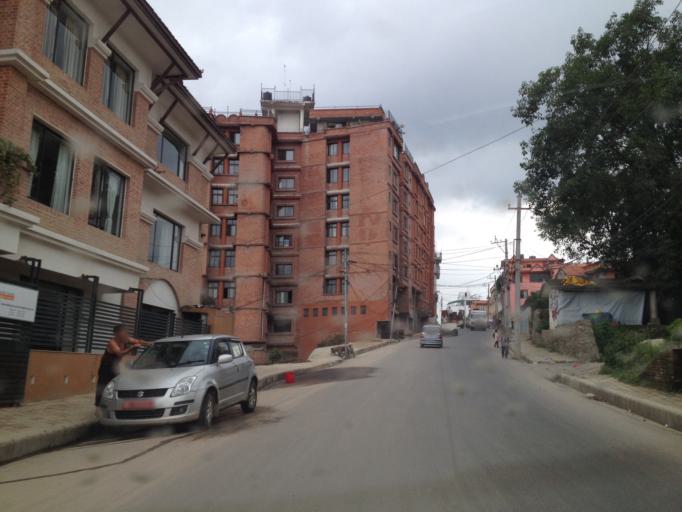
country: NP
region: Central Region
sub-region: Bagmati Zone
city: Kathmandu
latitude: 27.7029
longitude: 85.2996
